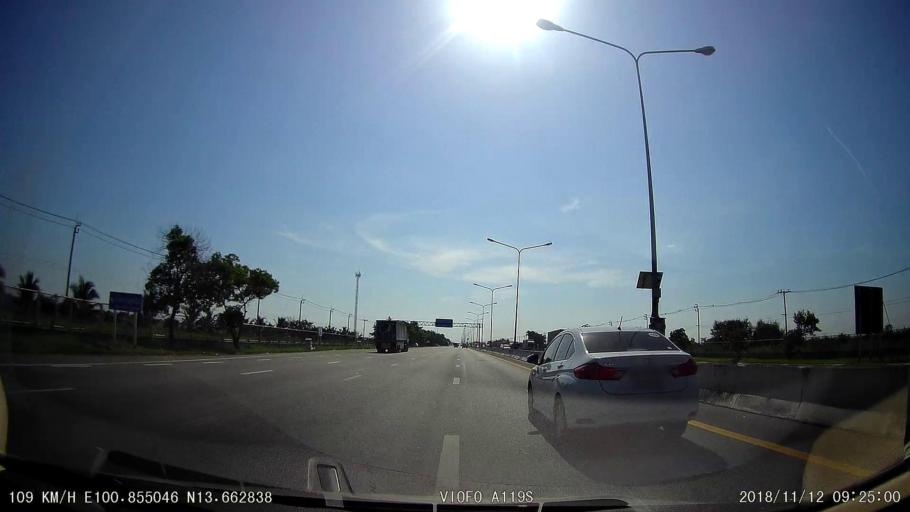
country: TH
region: Samut Prakan
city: Ban Khlong Bang Sao Thong
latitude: 13.6620
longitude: 100.8564
